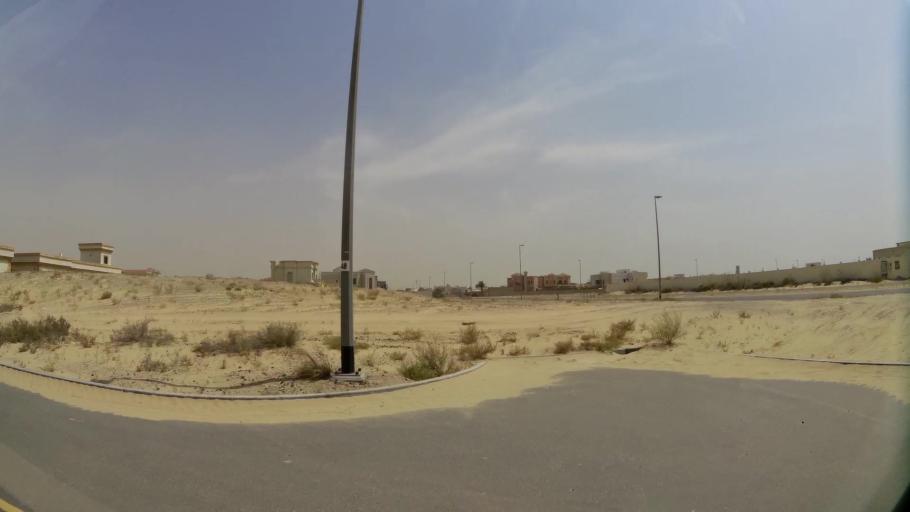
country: AE
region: Ash Shariqah
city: Sharjah
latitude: 25.2549
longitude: 55.4870
